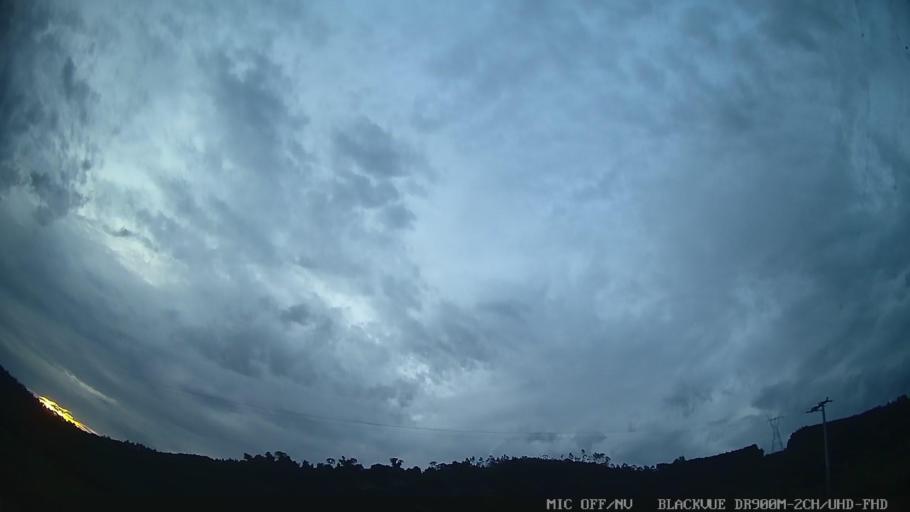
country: BR
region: Sao Paulo
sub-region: Amparo
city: Amparo
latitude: -22.8280
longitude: -46.7676
